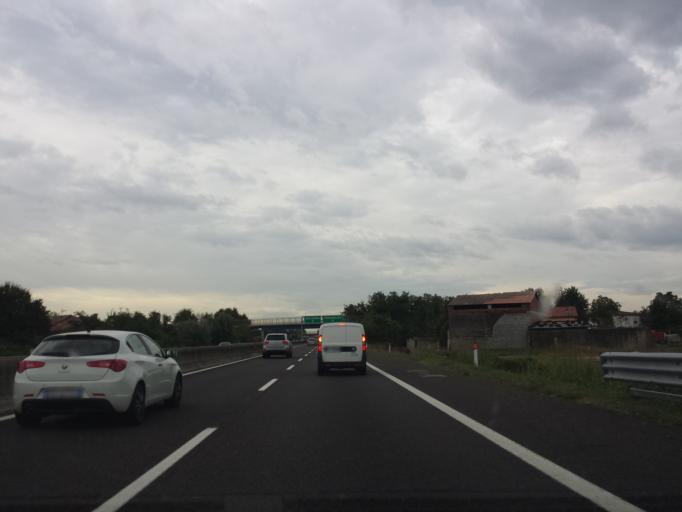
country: IT
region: Veneto
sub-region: Provincia di Padova
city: Pernumia
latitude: 45.2490
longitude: 11.7745
